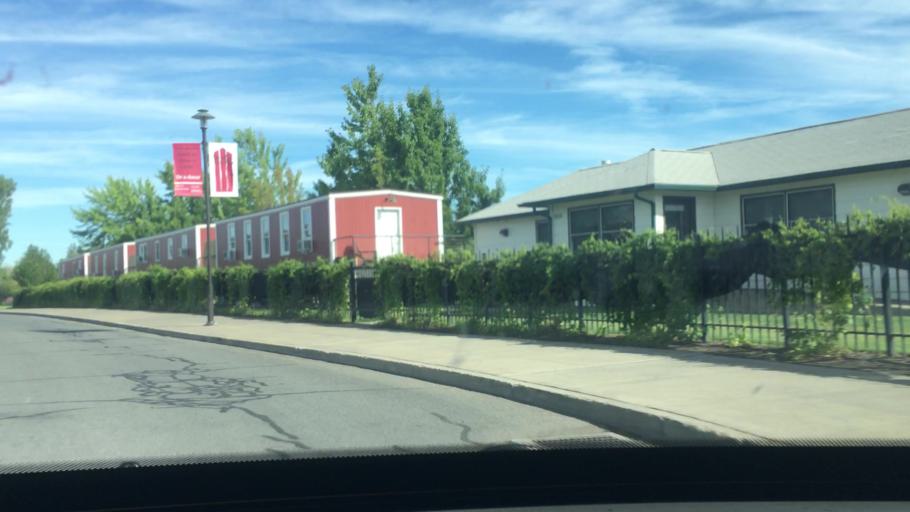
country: US
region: Oregon
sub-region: Deschutes County
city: Bend
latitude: 44.0473
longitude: -121.3188
